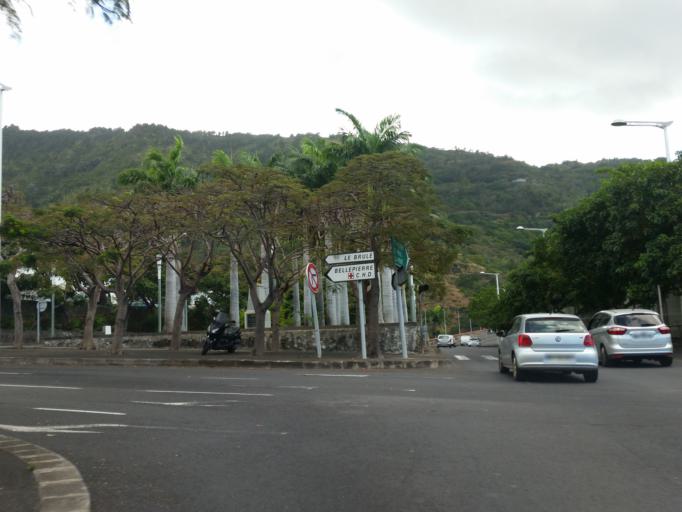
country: RE
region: Reunion
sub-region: Reunion
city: Saint-Denis
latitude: -20.8884
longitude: 55.4457
